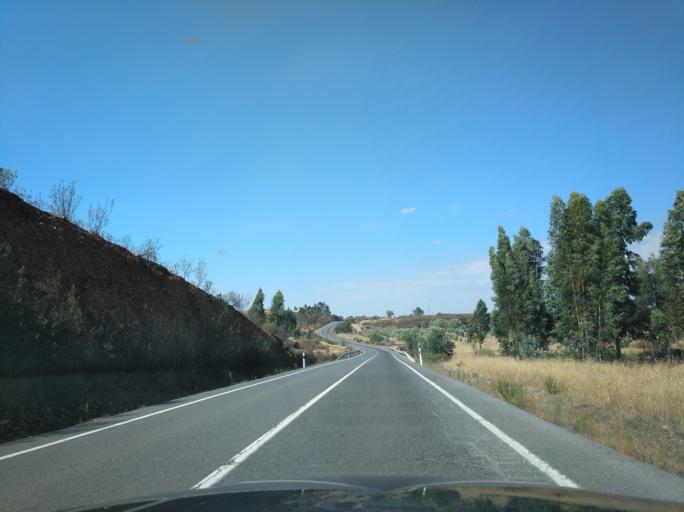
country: ES
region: Andalusia
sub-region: Provincia de Huelva
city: San Bartolome de la Torre
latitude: 37.4902
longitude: -7.1325
